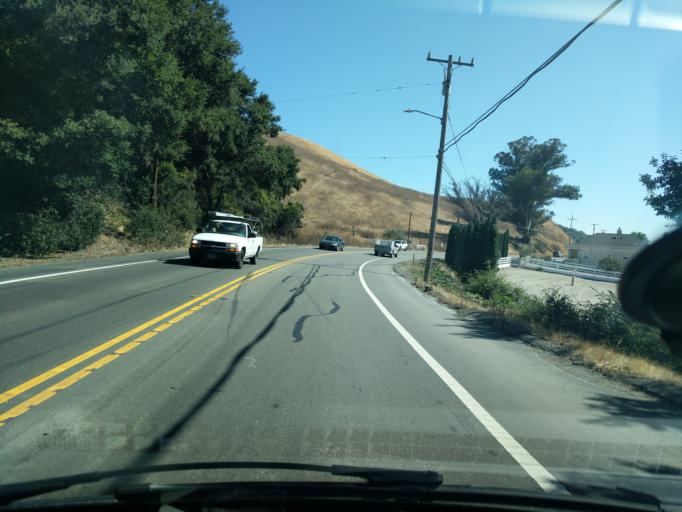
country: US
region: California
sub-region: Alameda County
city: Fairview
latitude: 37.7301
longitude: -122.0339
